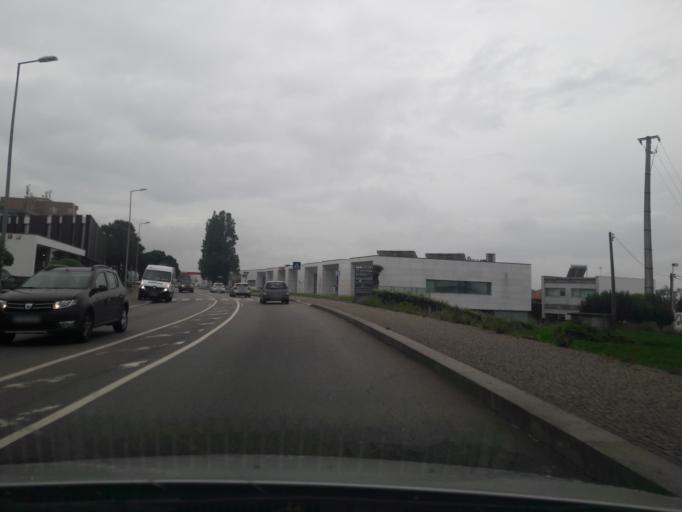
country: PT
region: Porto
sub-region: Vila do Conde
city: Vila do Conde
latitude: 41.3431
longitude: -8.7358
